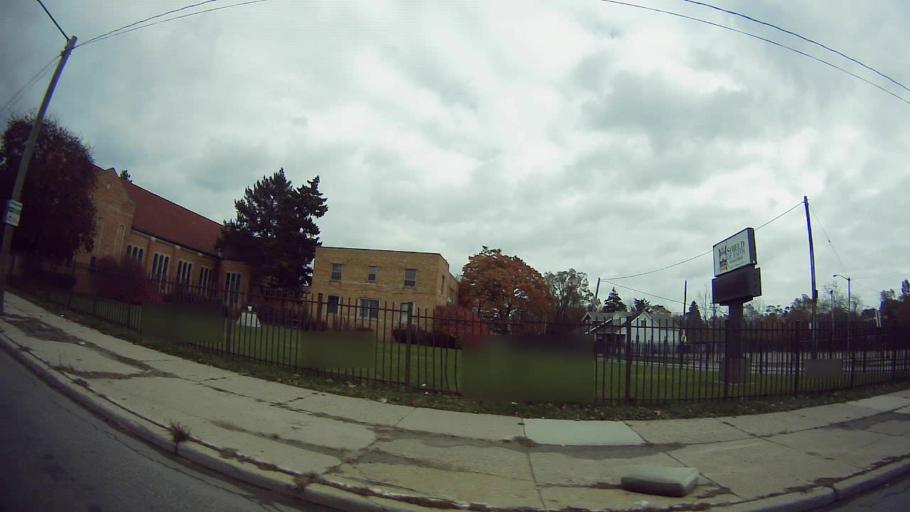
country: US
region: Michigan
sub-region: Wayne County
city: Hamtramck
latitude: 42.4170
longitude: -83.0235
